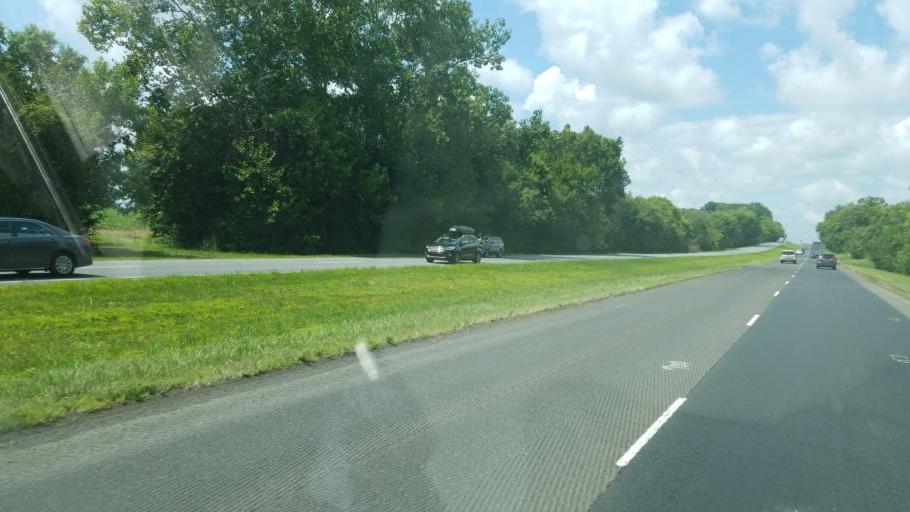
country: US
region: Virginia
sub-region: Fauquier County
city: Bealeton
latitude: 38.6027
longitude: -77.7789
